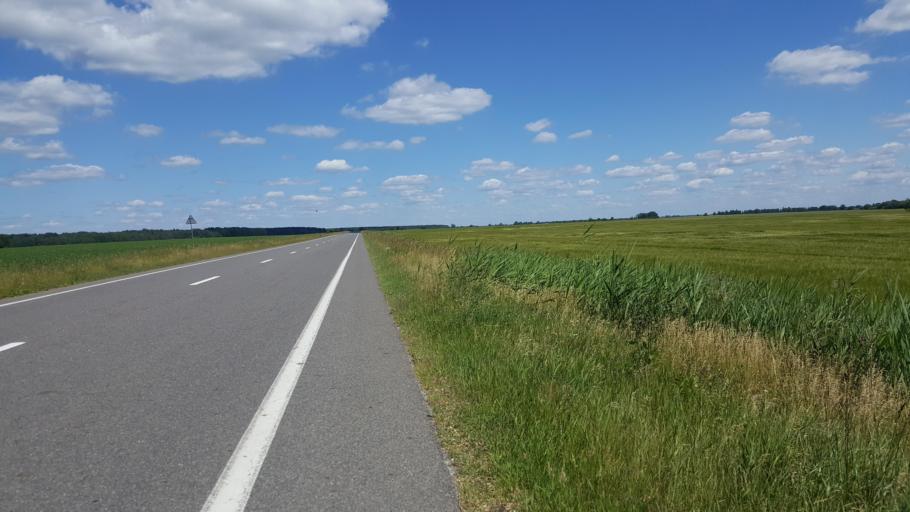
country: PL
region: Podlasie
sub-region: Powiat hajnowski
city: Czeremcha
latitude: 52.5053
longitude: 23.5077
